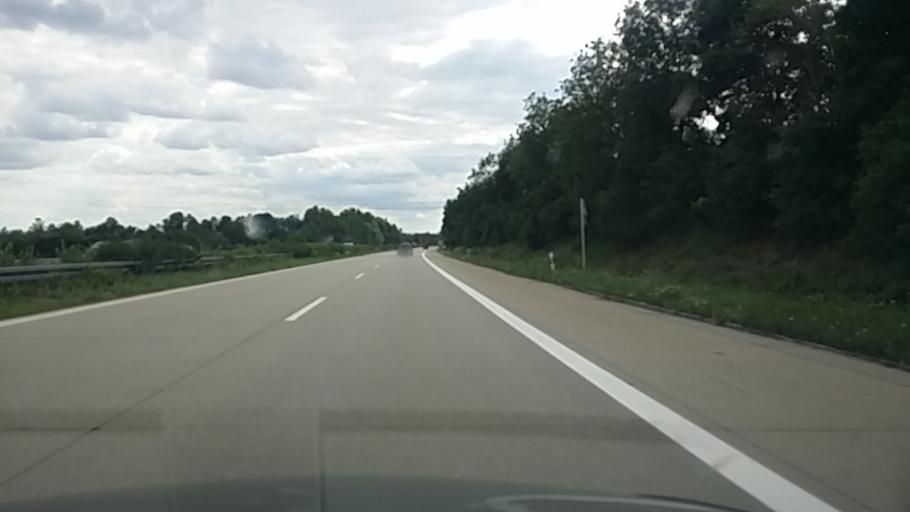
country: DE
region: Bavaria
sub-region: Lower Bavaria
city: Essenbach
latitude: 48.5934
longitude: 12.2160
